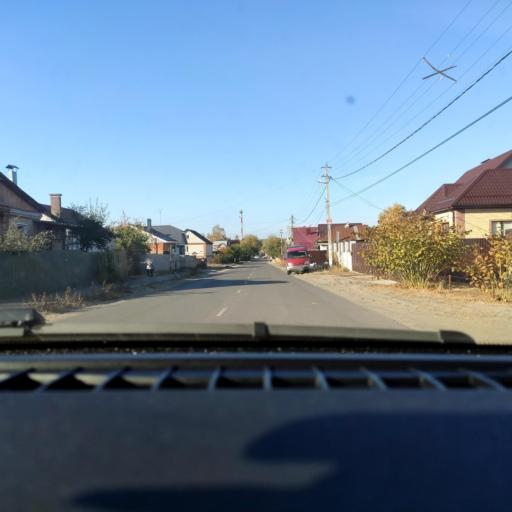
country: RU
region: Voronezj
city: Somovo
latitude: 51.7349
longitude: 39.2722
